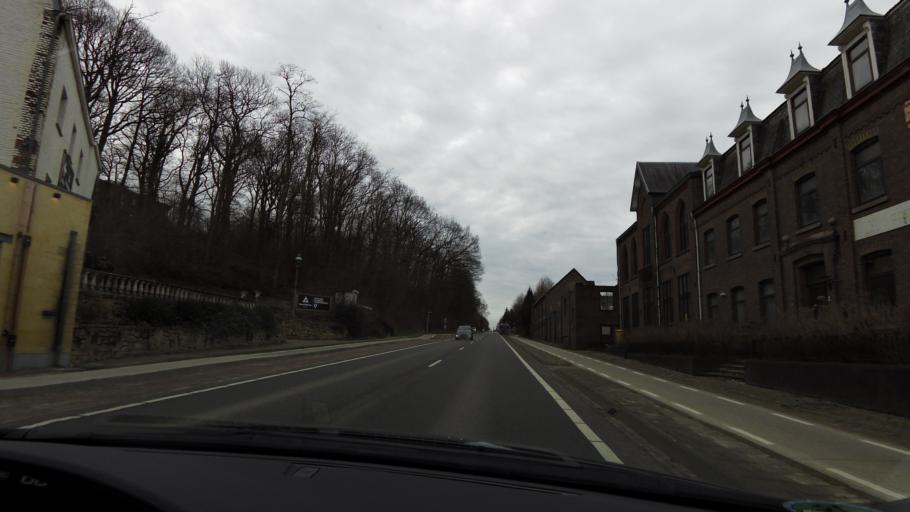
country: NL
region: Limburg
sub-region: Gemeente Maastricht
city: Heer
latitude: 50.8370
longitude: 5.7524
